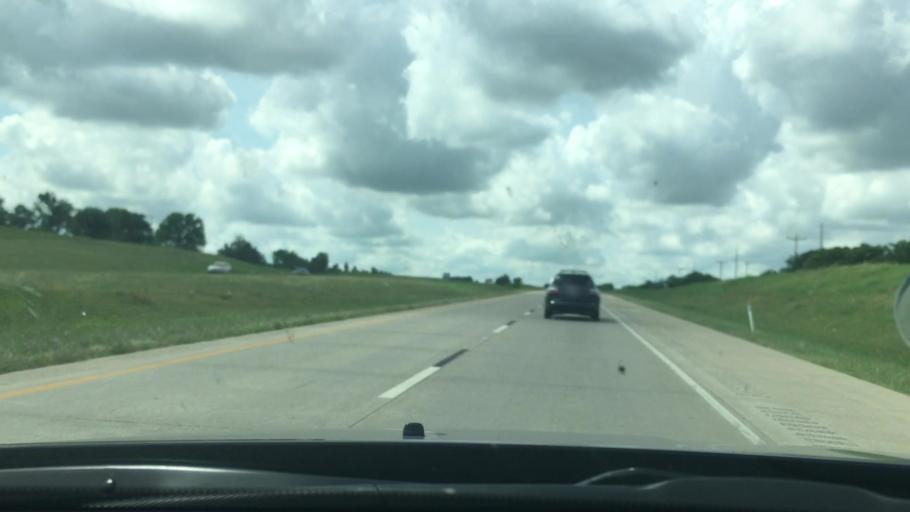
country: US
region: Oklahoma
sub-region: Love County
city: Marietta
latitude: 33.8721
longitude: -97.1344
